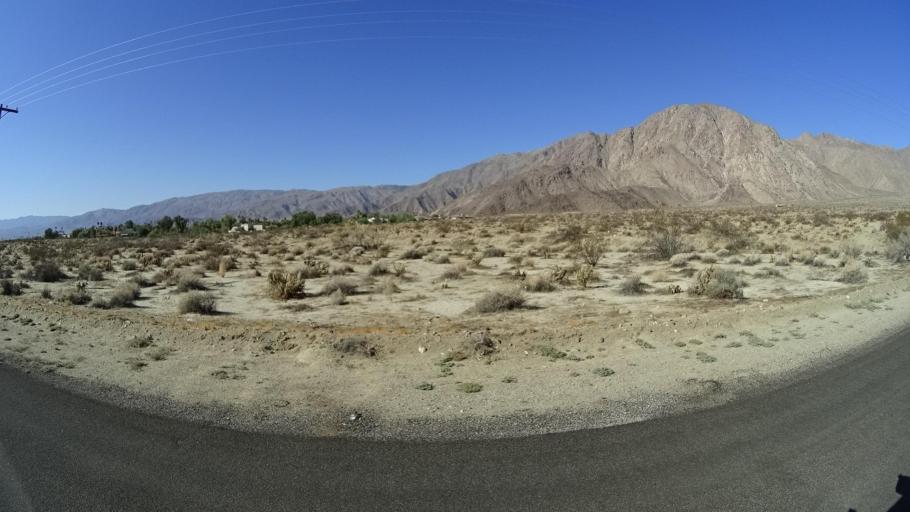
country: US
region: California
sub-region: San Diego County
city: Borrego Springs
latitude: 33.2999
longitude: -116.3862
